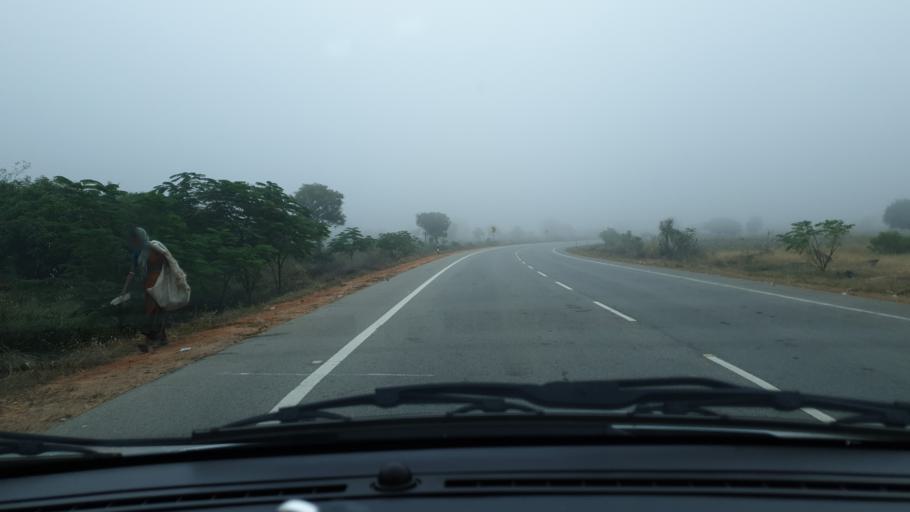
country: IN
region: Telangana
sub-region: Nalgonda
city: Devarkonda
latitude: 16.6233
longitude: 78.6704
